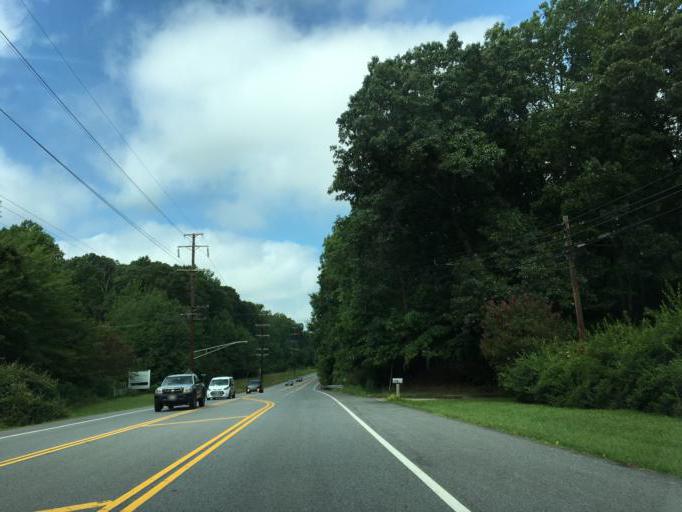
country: US
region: Maryland
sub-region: Anne Arundel County
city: Crownsville
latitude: 39.0152
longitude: -76.5757
